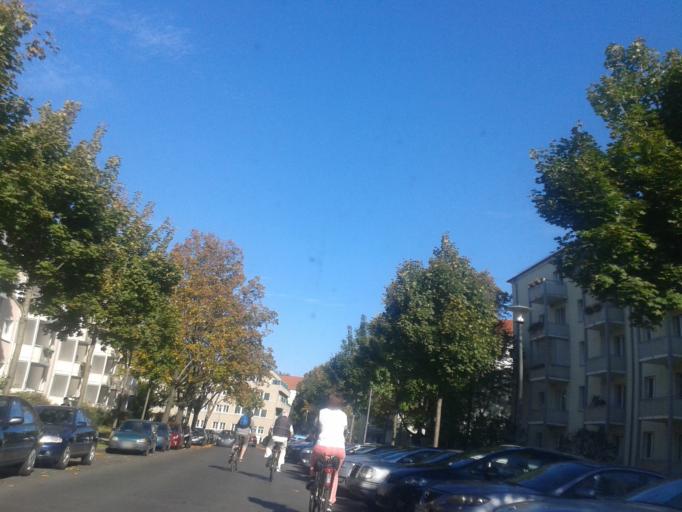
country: DE
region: Saxony
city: Albertstadt
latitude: 51.0481
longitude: 13.7770
